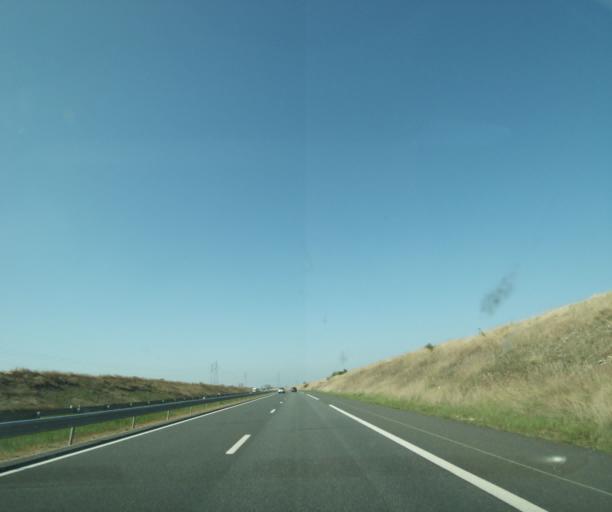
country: FR
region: Centre
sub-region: Departement du Loiret
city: Pannes
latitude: 48.0151
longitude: 2.6800
